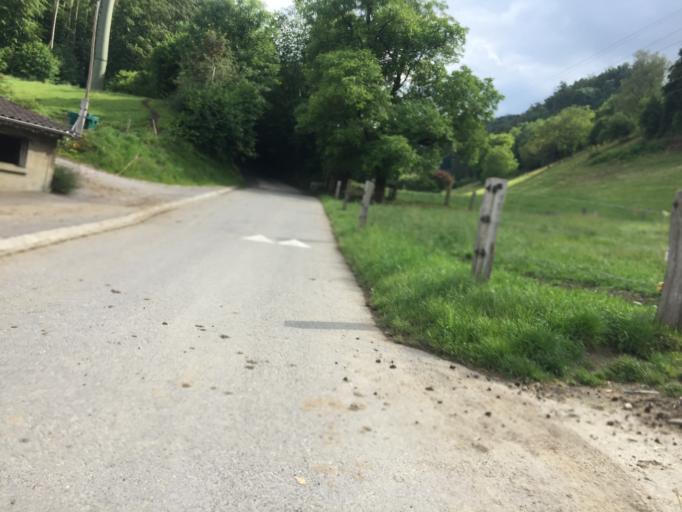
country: CH
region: Bern
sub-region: Bern-Mittelland District
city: Stettlen
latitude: 46.9566
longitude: 7.5122
